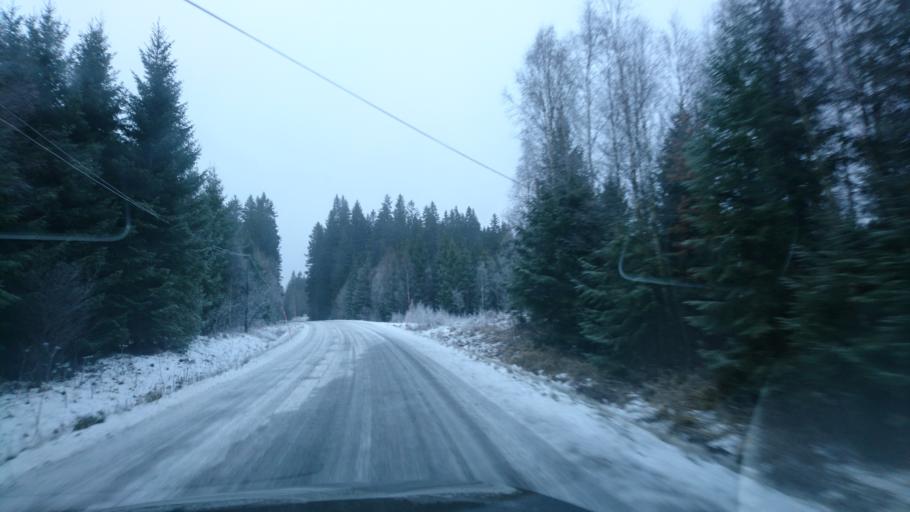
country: SE
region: Vaestra Goetaland
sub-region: Ulricehamns Kommun
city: Ulricehamn
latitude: 57.9659
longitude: 13.3990
